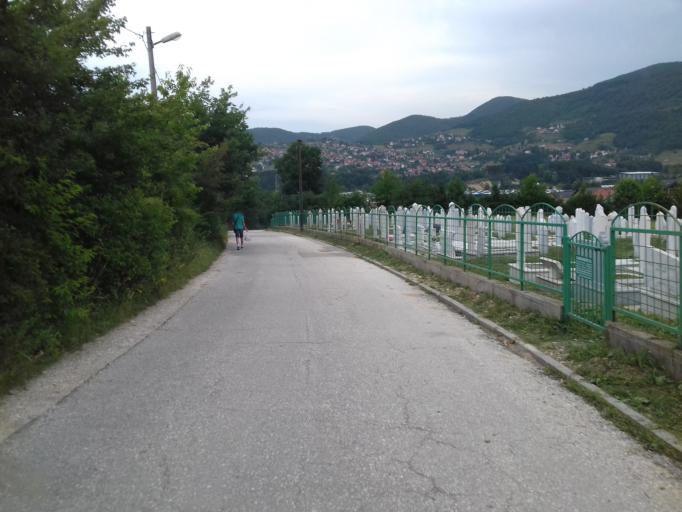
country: BA
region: Federation of Bosnia and Herzegovina
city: Hotonj
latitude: 43.8931
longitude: 18.3626
